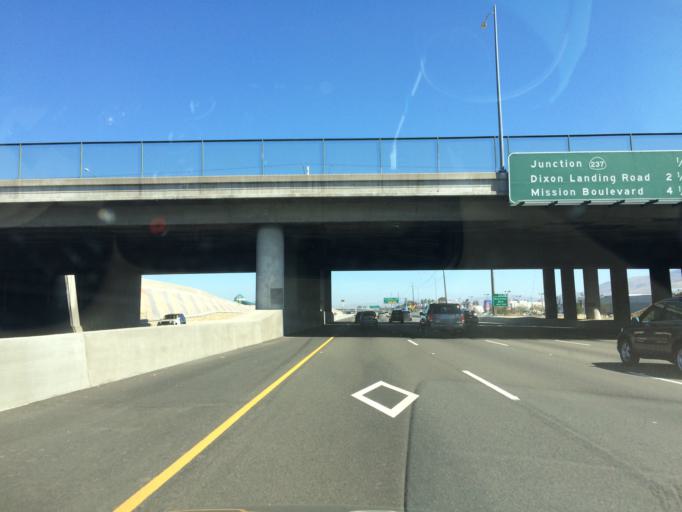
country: US
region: California
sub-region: Santa Clara County
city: Milpitas
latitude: 37.4148
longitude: -121.9127
